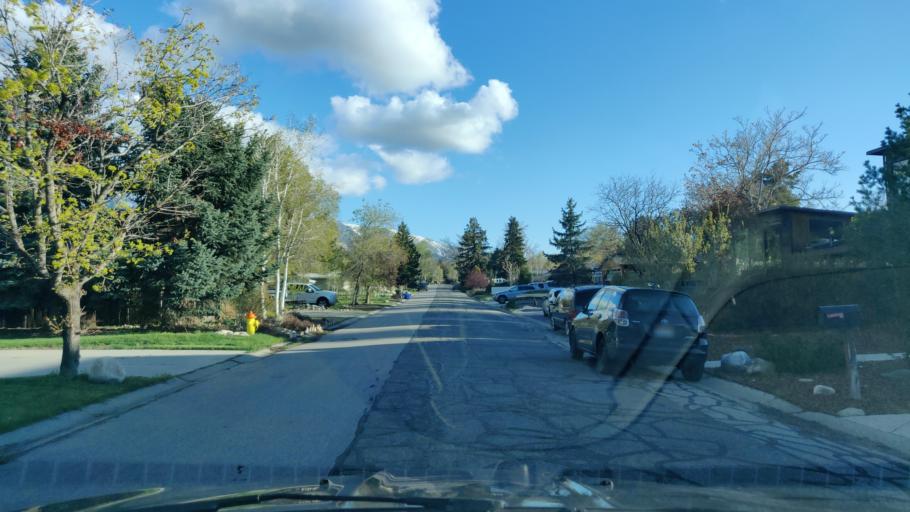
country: US
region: Utah
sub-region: Salt Lake County
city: Cottonwood Heights
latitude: 40.6221
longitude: -111.8098
